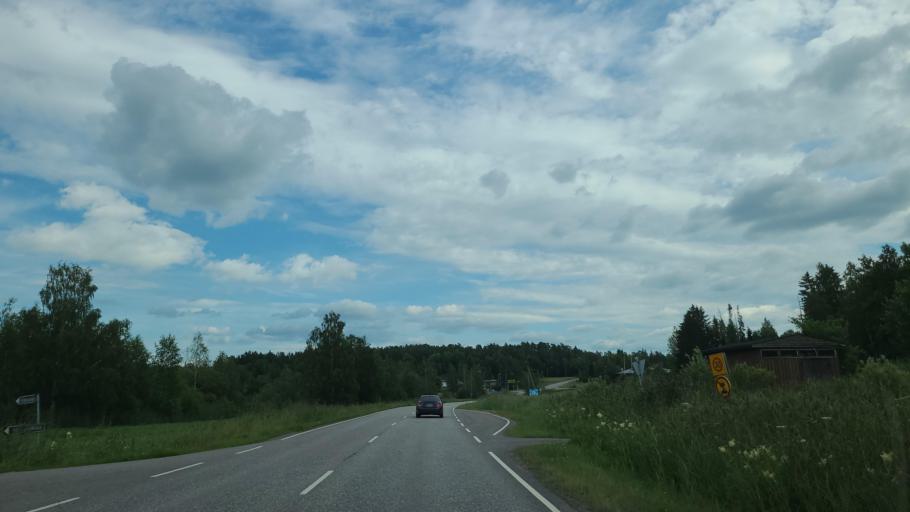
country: FI
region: Varsinais-Suomi
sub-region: Turku
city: Rymaettylae
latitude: 60.3798
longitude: 21.9428
